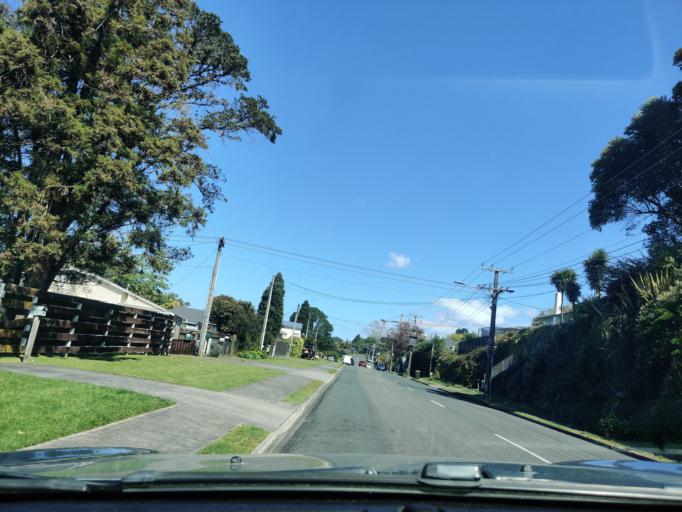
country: NZ
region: Taranaki
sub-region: New Plymouth District
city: New Plymouth
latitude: -39.0644
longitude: 174.0540
